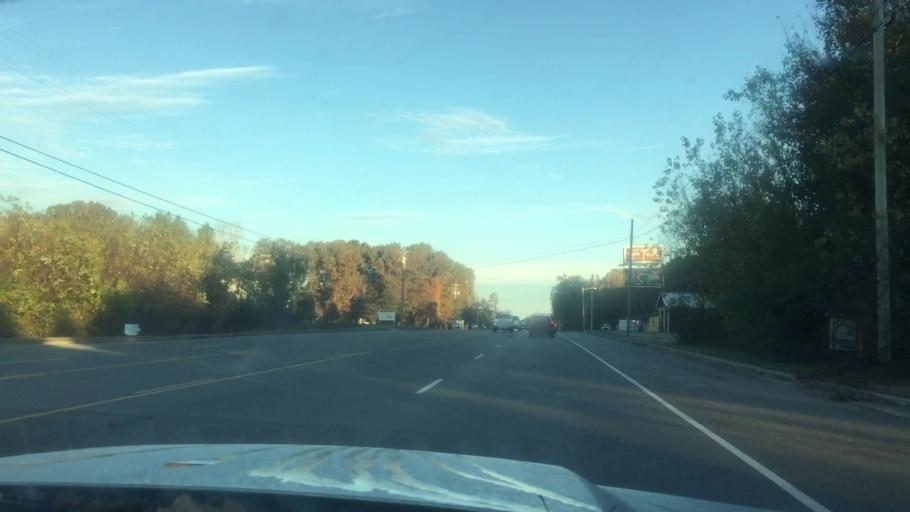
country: US
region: Tennessee
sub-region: Franklin County
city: Estill Springs
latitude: 35.2868
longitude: -86.1424
